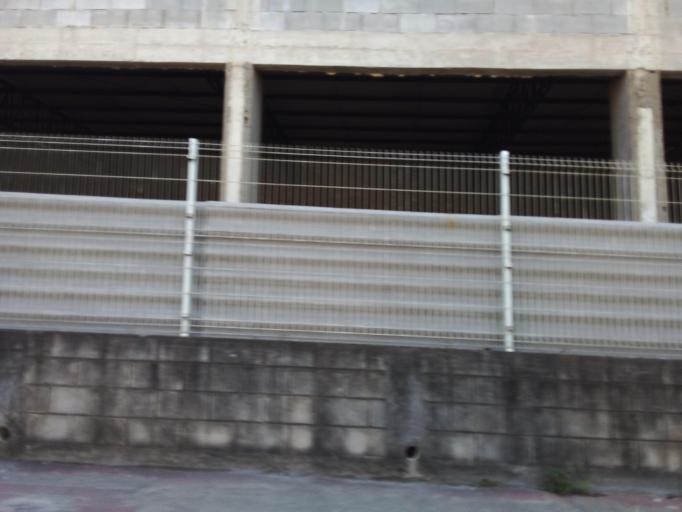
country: BR
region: Espirito Santo
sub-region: Vitoria
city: Vitoria
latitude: -20.3111
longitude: -40.3698
